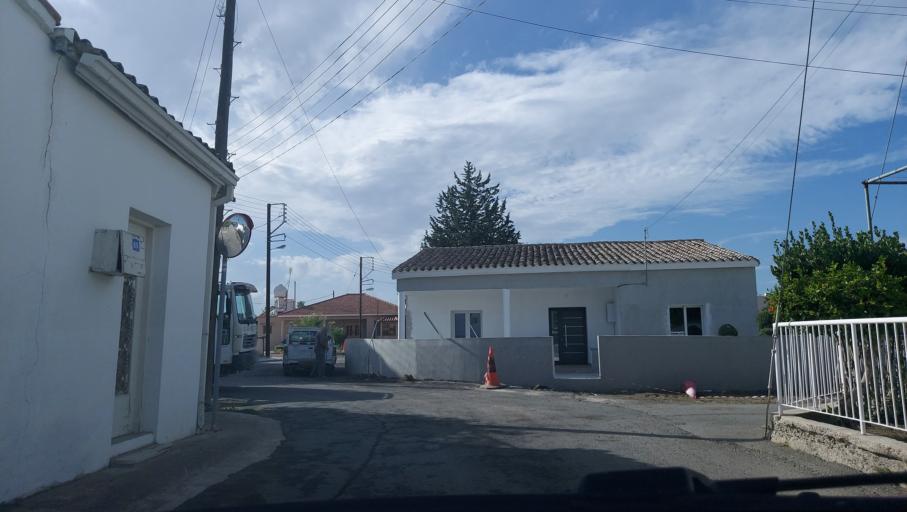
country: CY
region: Lefkosia
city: Pano Deftera
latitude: 35.0826
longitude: 33.2657
